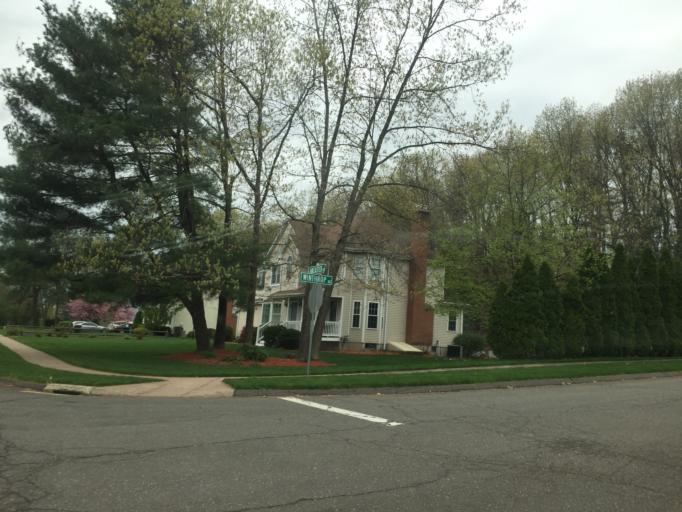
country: US
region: Connecticut
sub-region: Hartford County
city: Glastonbury
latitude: 41.7284
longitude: -72.5942
